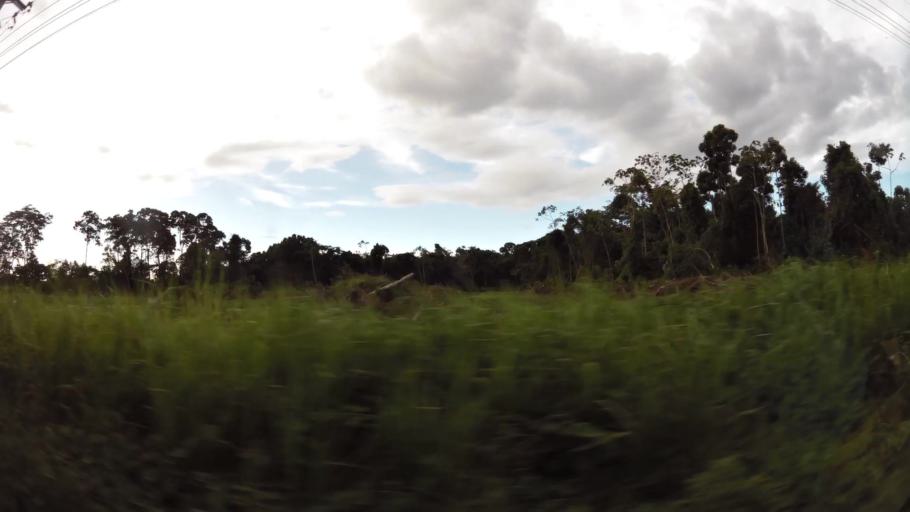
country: SR
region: Paramaribo
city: Paramaribo
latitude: 5.8582
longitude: -55.1780
